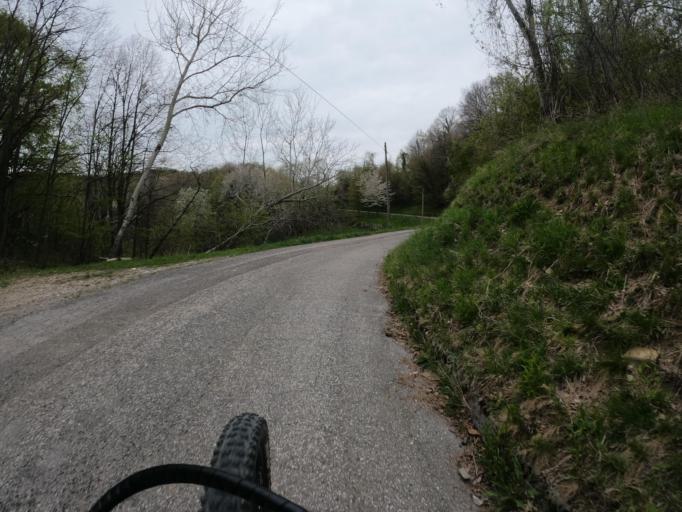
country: IT
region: Friuli Venezia Giulia
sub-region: Provincia di Udine
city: Stregna
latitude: 46.1270
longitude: 13.6112
